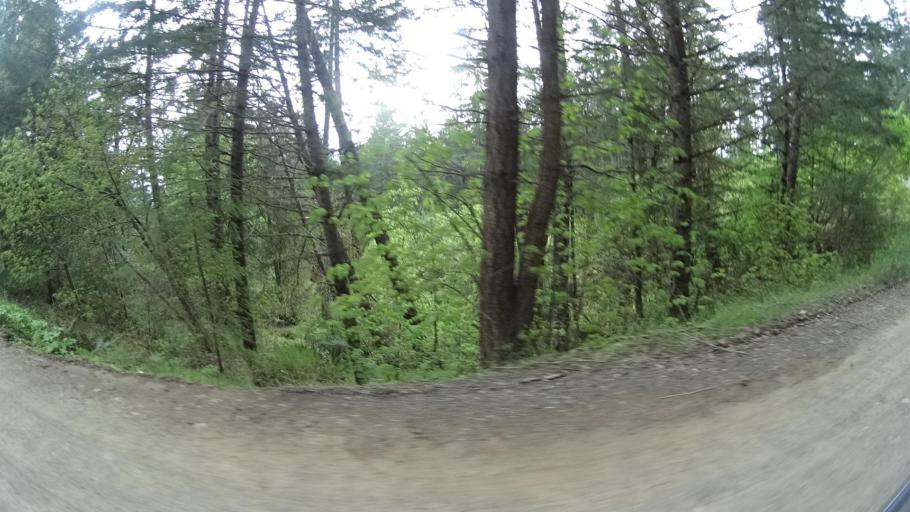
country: US
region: California
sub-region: Humboldt County
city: Redway
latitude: 40.2587
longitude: -123.7677
